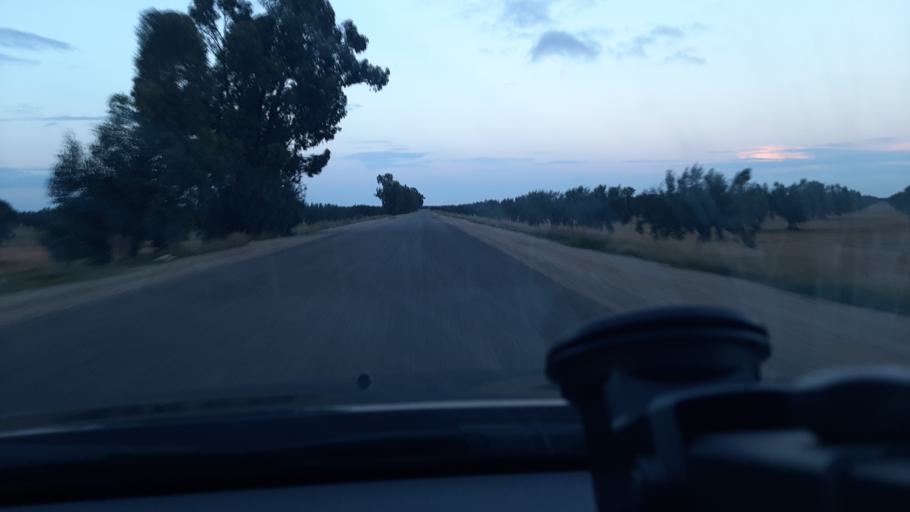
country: TN
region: Al Mahdiyah
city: Shurban
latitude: 34.9785
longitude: 10.3810
